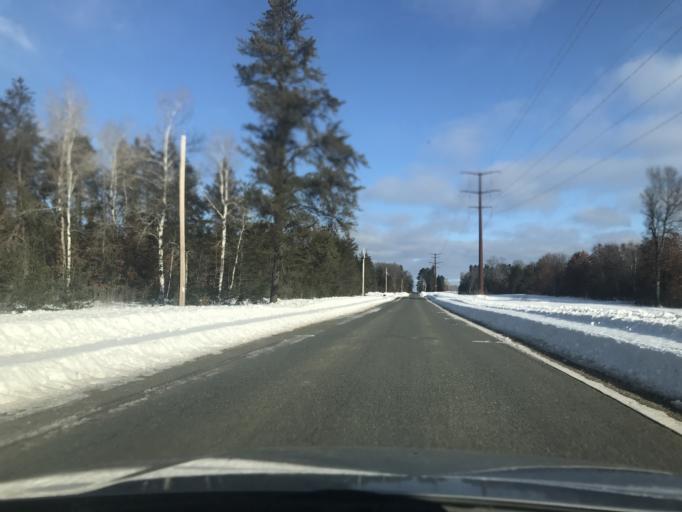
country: US
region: Wisconsin
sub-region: Marinette County
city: Niagara
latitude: 45.5997
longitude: -87.9769
